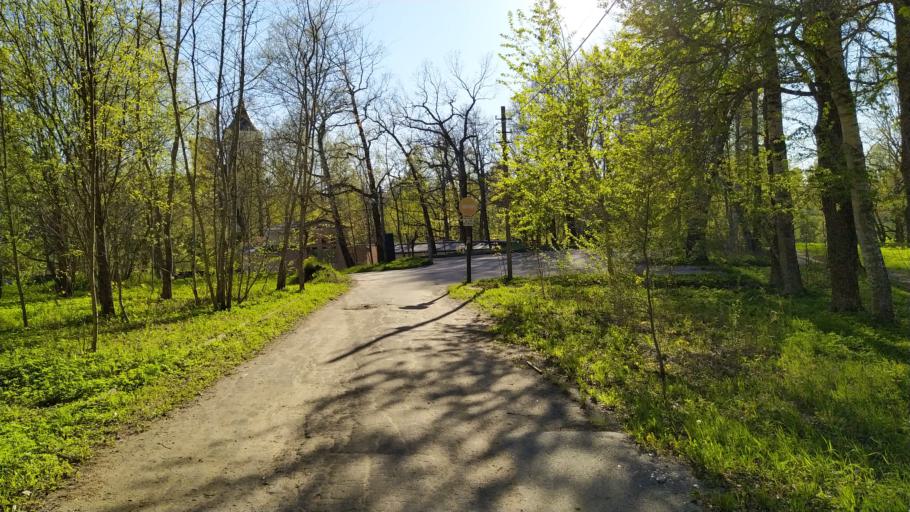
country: RU
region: St.-Petersburg
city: Pavlovsk
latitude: 59.6815
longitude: 30.4466
